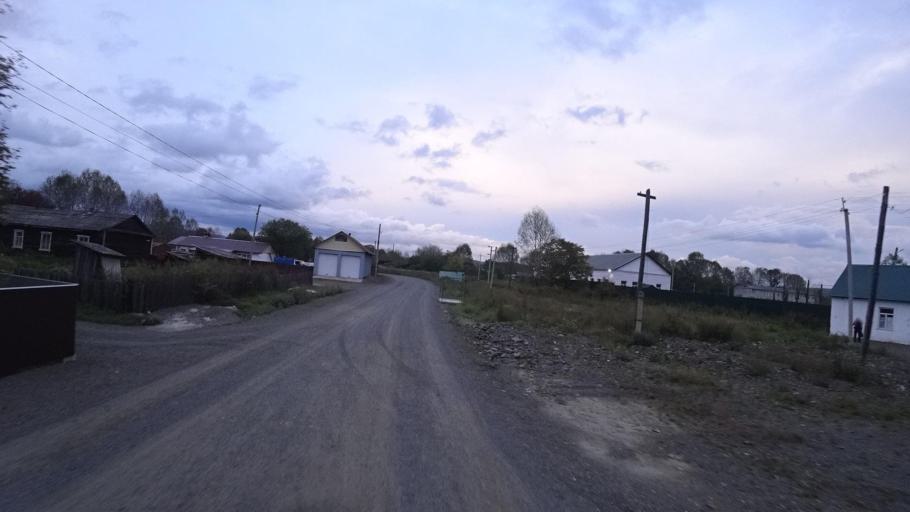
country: RU
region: Jewish Autonomous Oblast
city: Izvestkovyy
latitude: 48.9881
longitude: 131.5526
